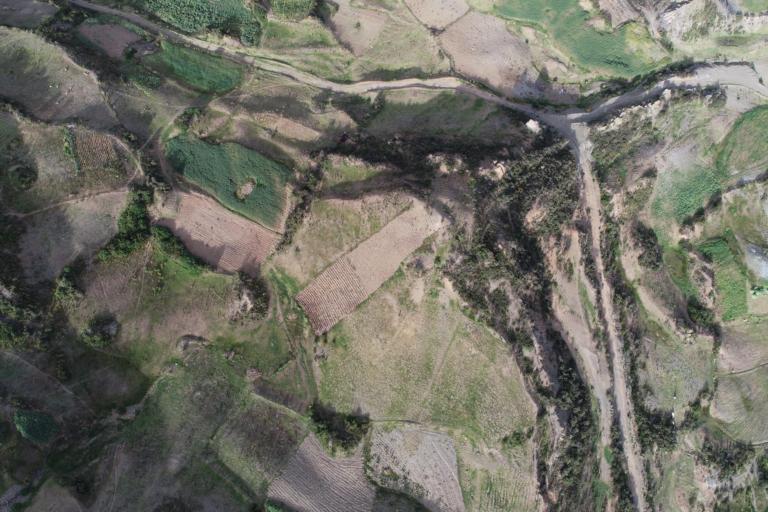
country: BO
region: La Paz
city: La Paz
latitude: -16.5494
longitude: -67.9990
